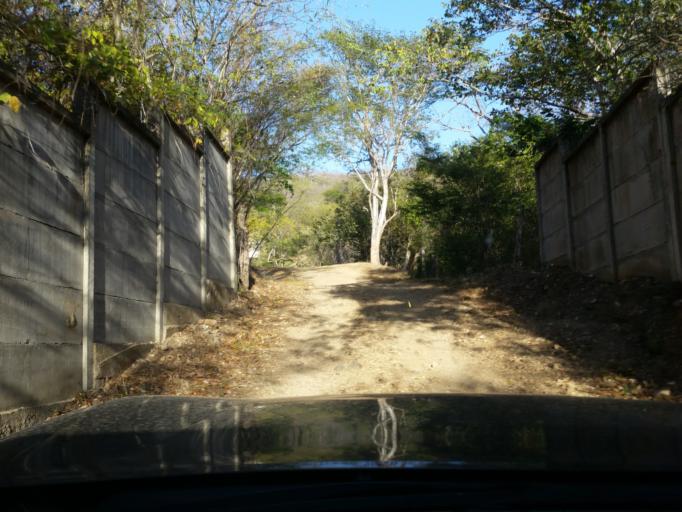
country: NI
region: Rivas
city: San Juan del Sur
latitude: 11.1796
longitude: -85.8112
